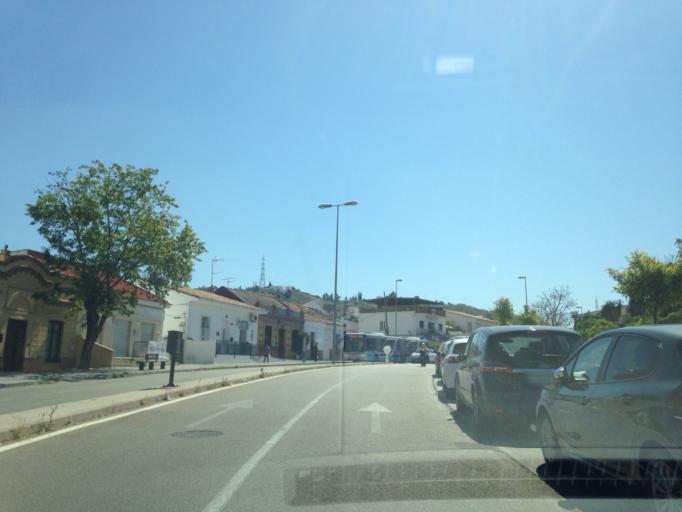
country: ES
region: Andalusia
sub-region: Provincia de Malaga
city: Malaga
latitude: 36.7400
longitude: -4.4825
